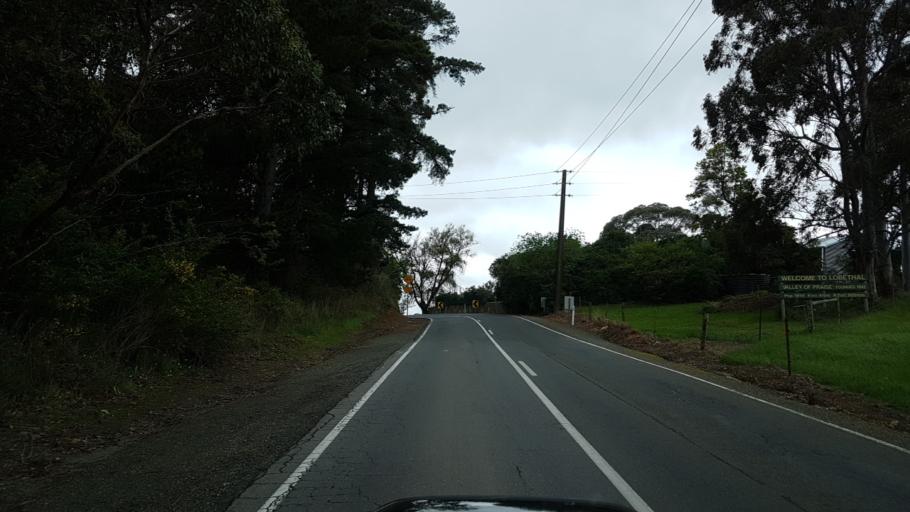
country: AU
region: South Australia
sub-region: Adelaide Hills
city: Lobethal
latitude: -34.9120
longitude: 138.8683
